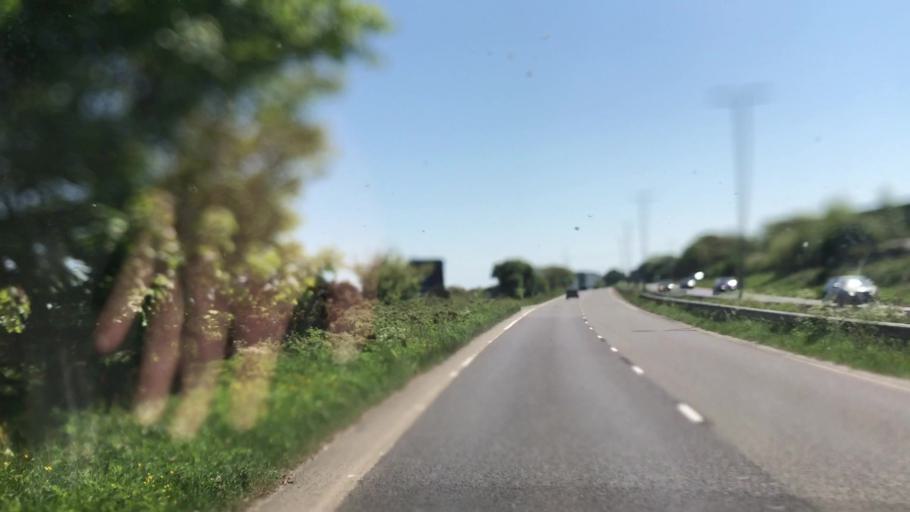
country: GB
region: England
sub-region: Cornwall
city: Chacewater
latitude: 50.2644
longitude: -5.1120
